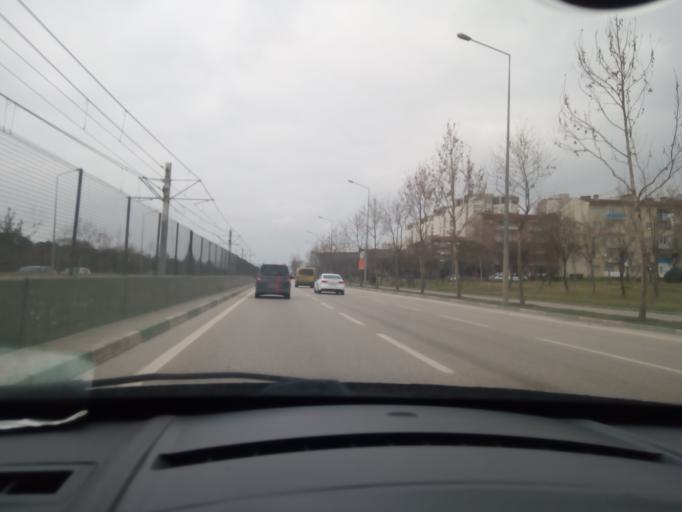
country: TR
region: Bursa
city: Niluefer
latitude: 40.2465
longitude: 28.9631
